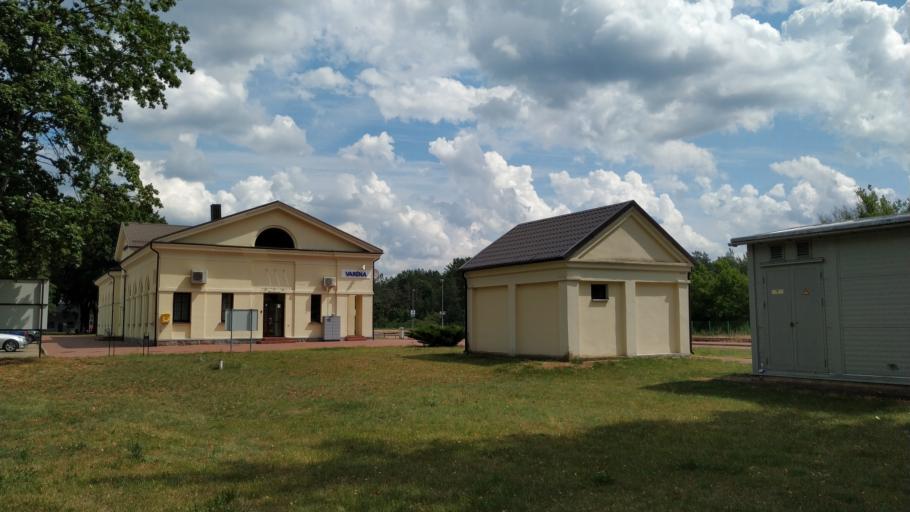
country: LT
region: Alytaus apskritis
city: Varena
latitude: 54.2093
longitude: 24.5737
